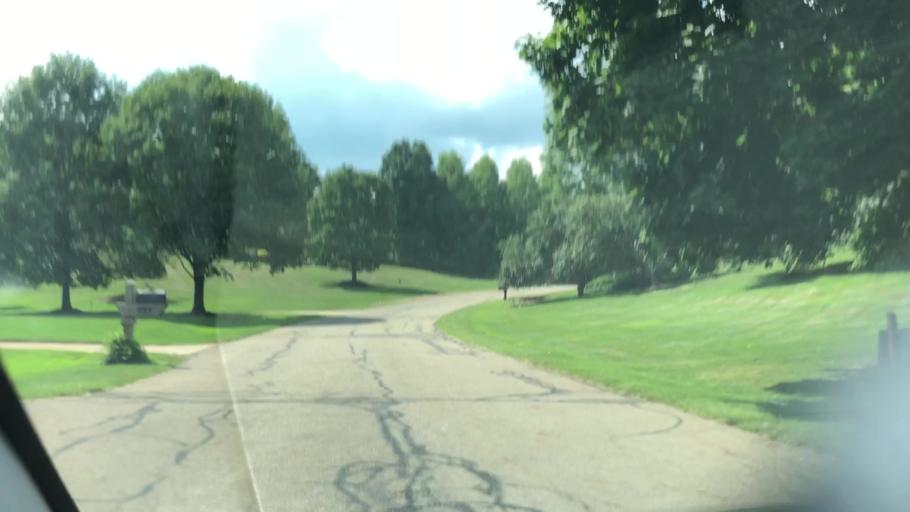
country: US
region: Ohio
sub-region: Summit County
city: Montrose-Ghent
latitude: 41.1594
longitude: -81.6407
